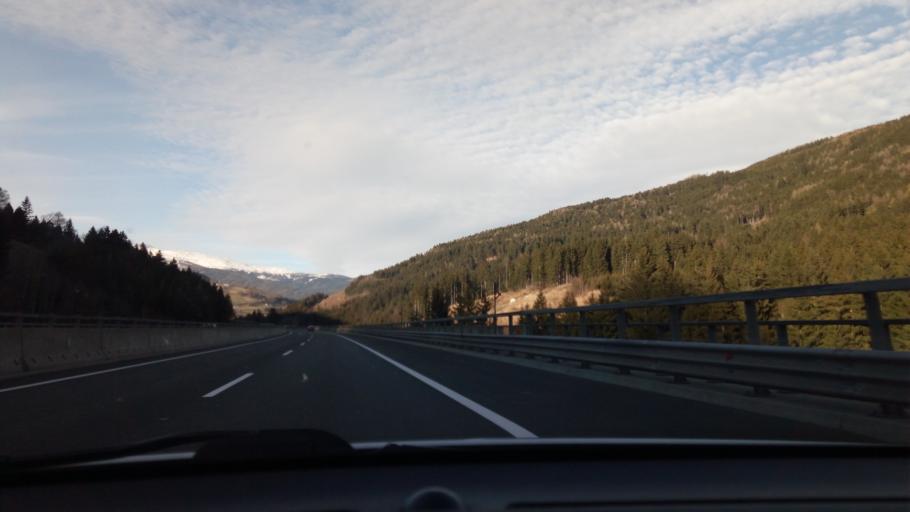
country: AT
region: Carinthia
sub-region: Politischer Bezirk Spittal an der Drau
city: Trebesing
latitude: 46.8581
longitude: 13.5016
